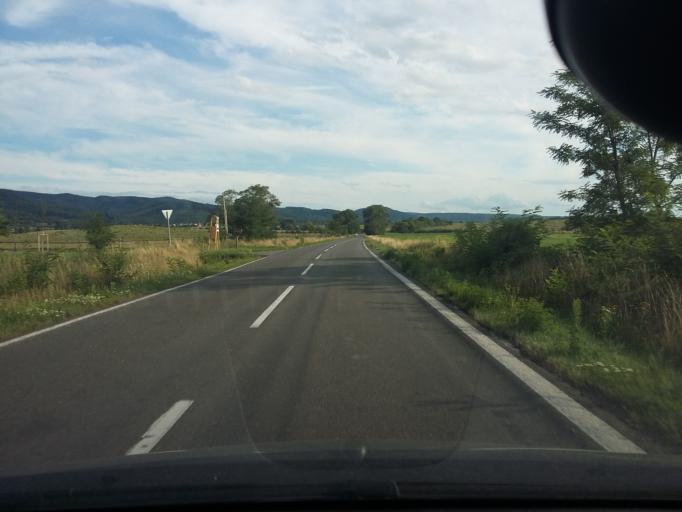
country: SK
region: Bratislavsky
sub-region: Okres Malacky
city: Malacky
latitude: 48.4260
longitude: 17.1599
